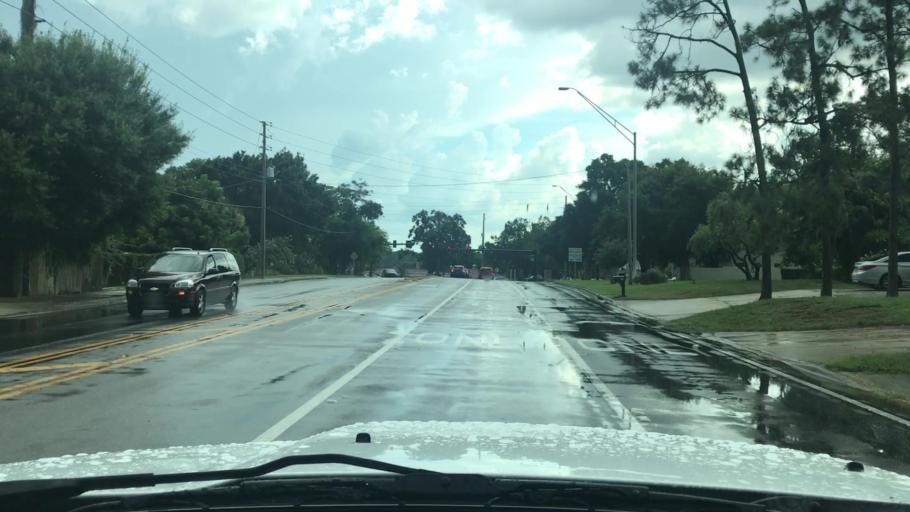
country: US
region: Florida
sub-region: Polk County
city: Cypress Gardens
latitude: 28.0036
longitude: -81.6912
